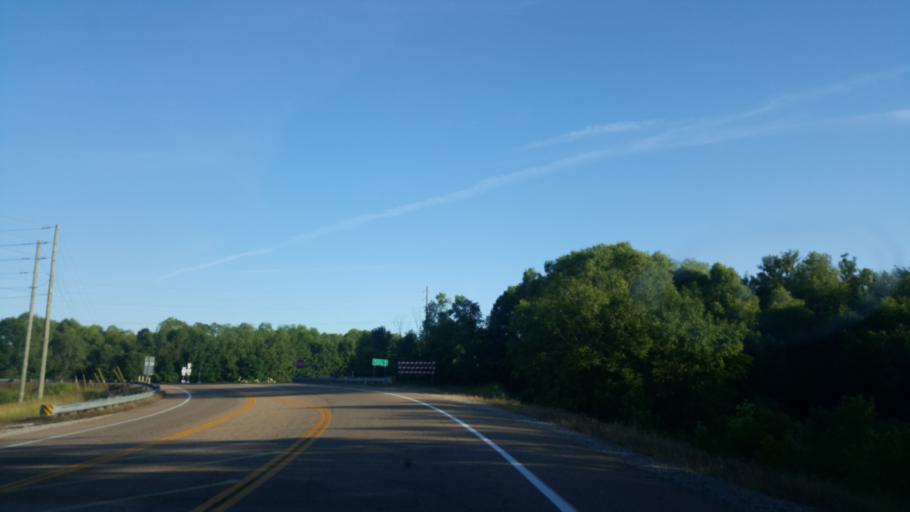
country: US
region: Tennessee
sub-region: McNairy County
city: Adamsville
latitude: 35.3574
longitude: -88.3658
